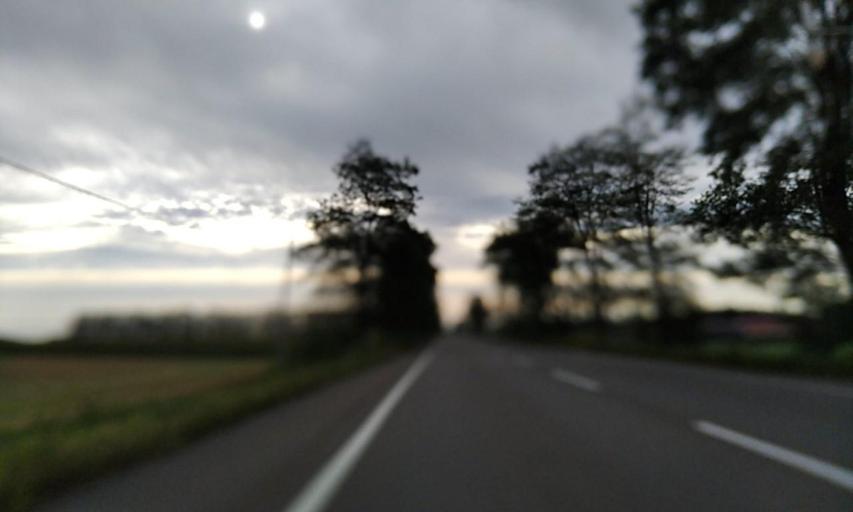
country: JP
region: Hokkaido
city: Obihiro
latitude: 42.9266
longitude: 142.9859
